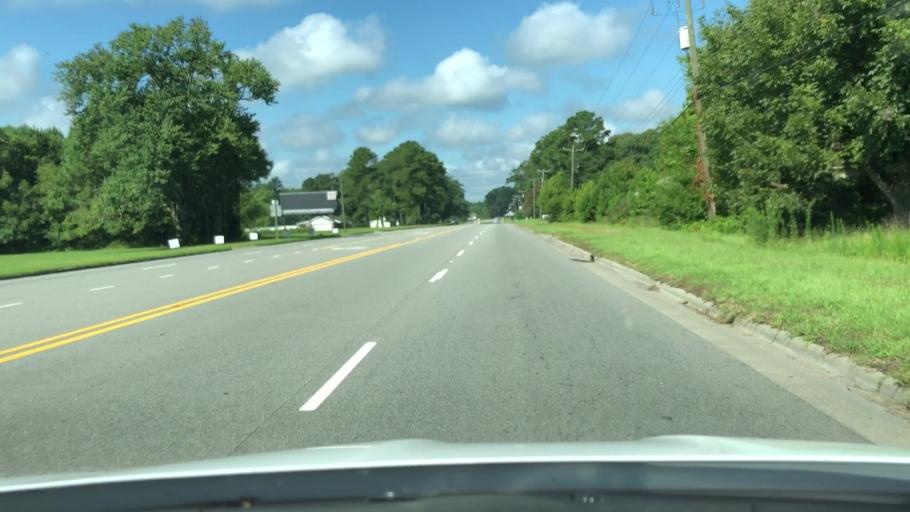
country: US
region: North Carolina
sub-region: Bertie County
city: Windsor
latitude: 36.0343
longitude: -76.7858
